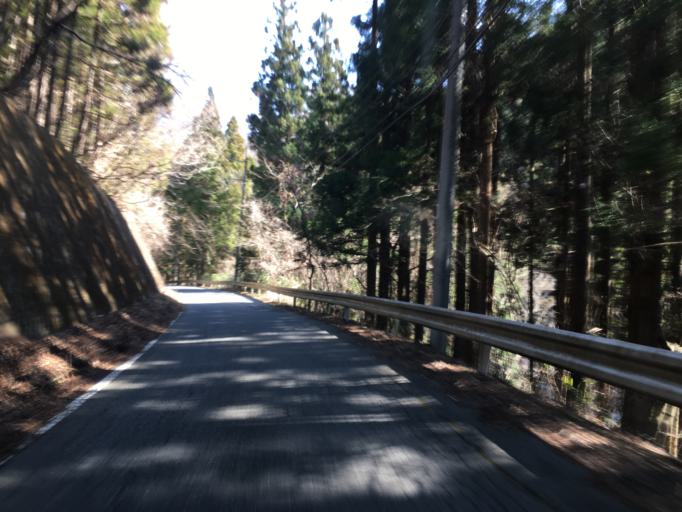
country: JP
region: Ibaraki
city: Takahagi
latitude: 36.8029
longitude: 140.6098
